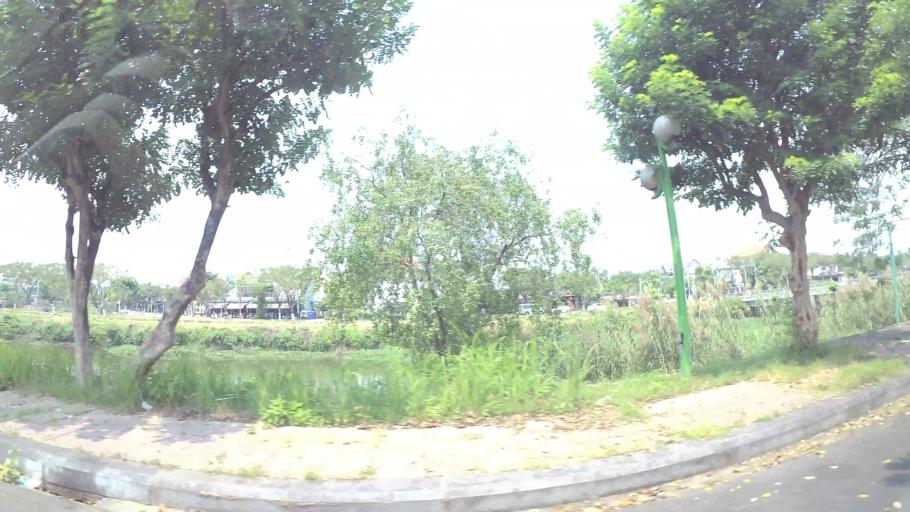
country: VN
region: Da Nang
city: Cam Le
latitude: 16.0144
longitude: 108.2100
